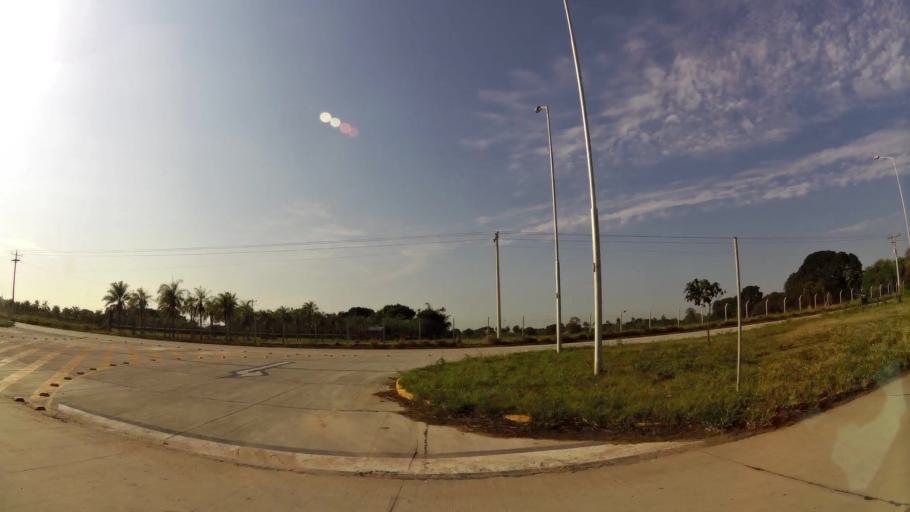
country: BO
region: Santa Cruz
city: Santa Cruz de la Sierra
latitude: -17.6972
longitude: -63.1238
